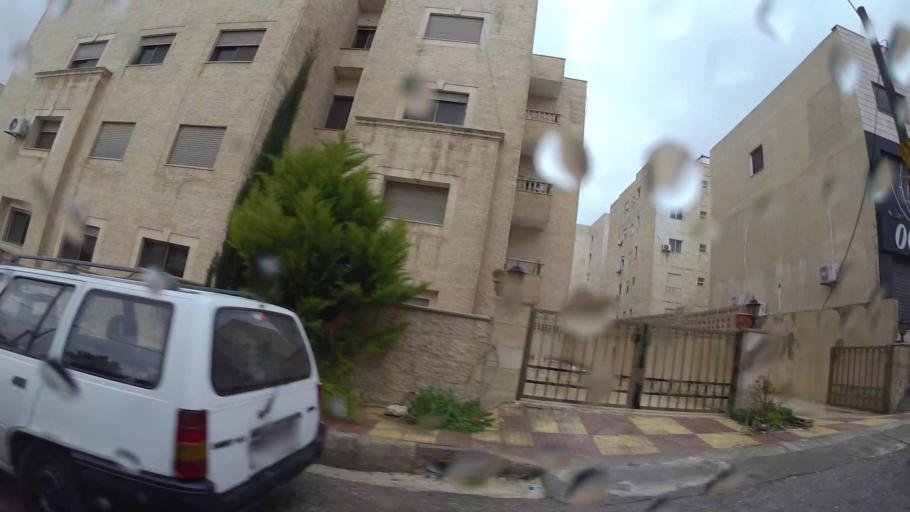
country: JO
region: Amman
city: Al Jubayhah
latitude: 32.0248
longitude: 35.8683
